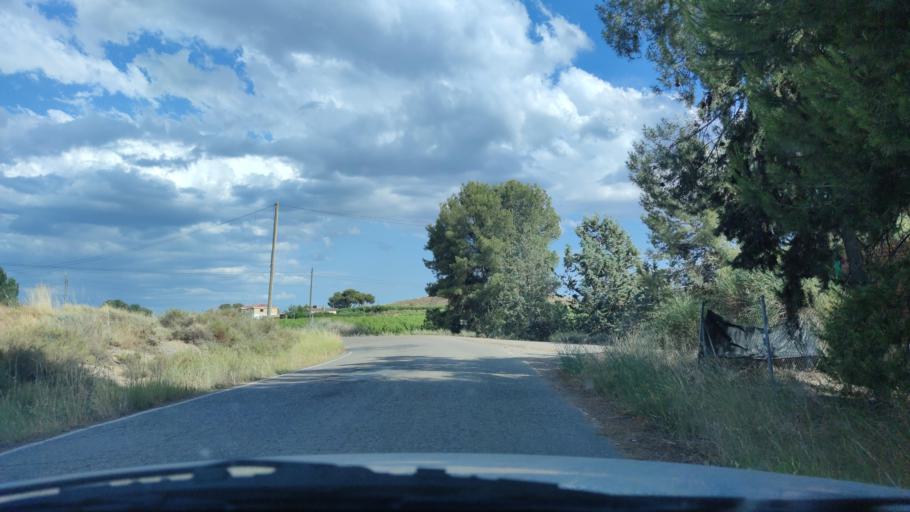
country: ES
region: Catalonia
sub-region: Provincia de Lleida
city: Alpicat
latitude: 41.6286
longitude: 0.5707
